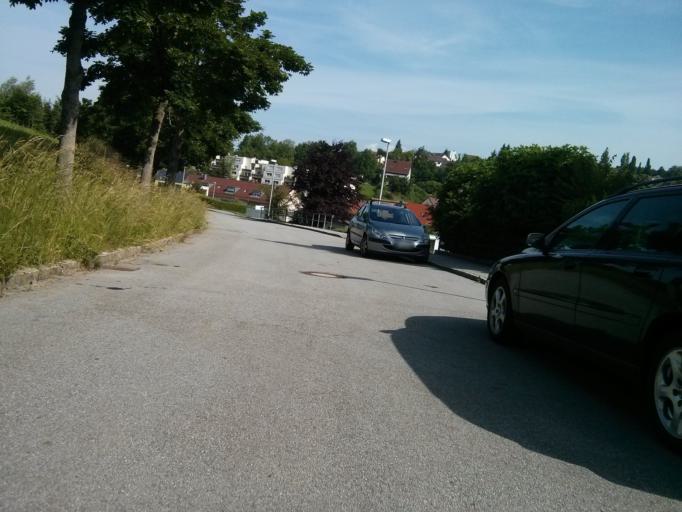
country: DE
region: Bavaria
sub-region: Lower Bavaria
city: Deggendorf
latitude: 48.8313
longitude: 12.9731
